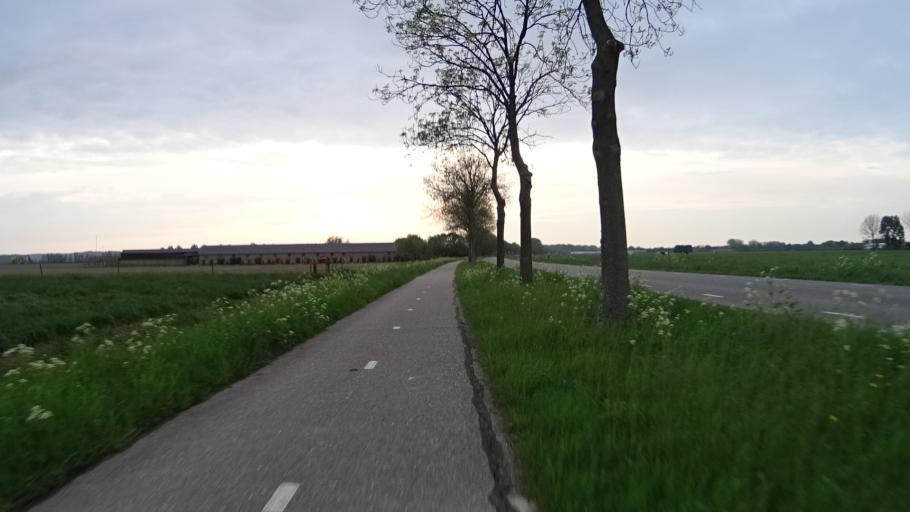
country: NL
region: North Brabant
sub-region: Gemeente Woudrichem
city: Woudrichem
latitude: 51.7783
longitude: 5.0489
